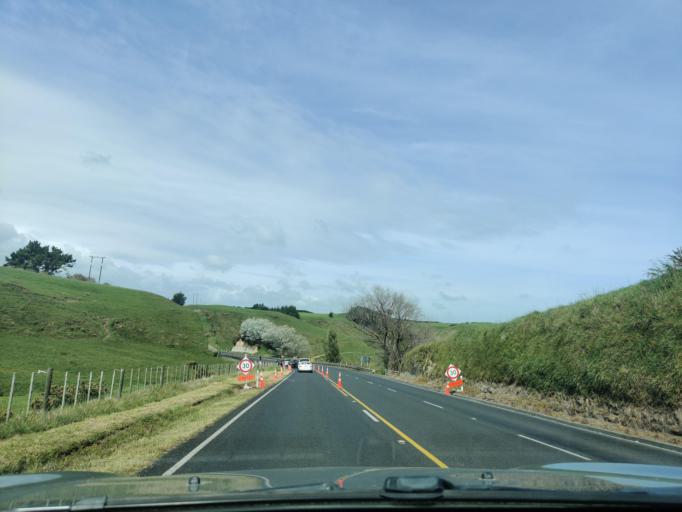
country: NZ
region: Taranaki
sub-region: South Taranaki District
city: Hawera
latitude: -39.6176
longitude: 174.3412
